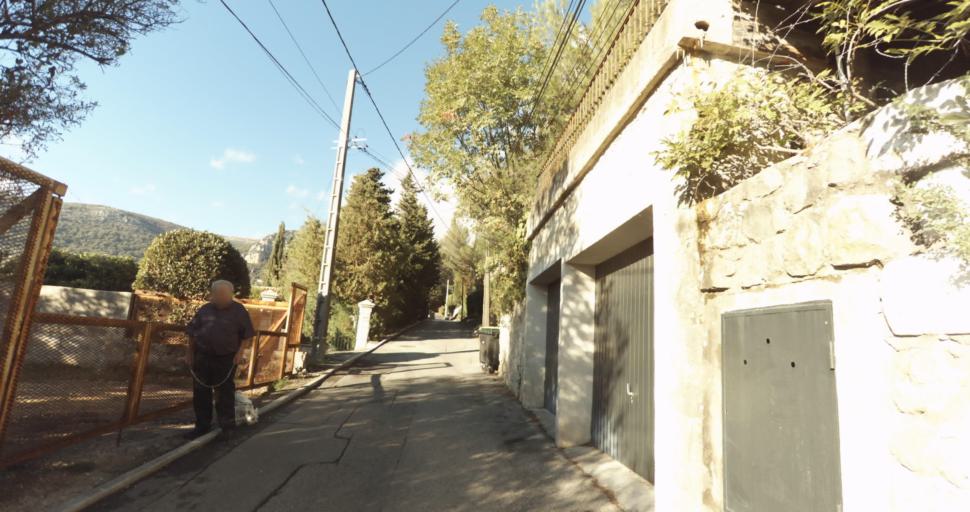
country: FR
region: Provence-Alpes-Cote d'Azur
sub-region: Departement des Alpes-Maritimes
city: La Gaude
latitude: 43.7281
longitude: 7.1342
